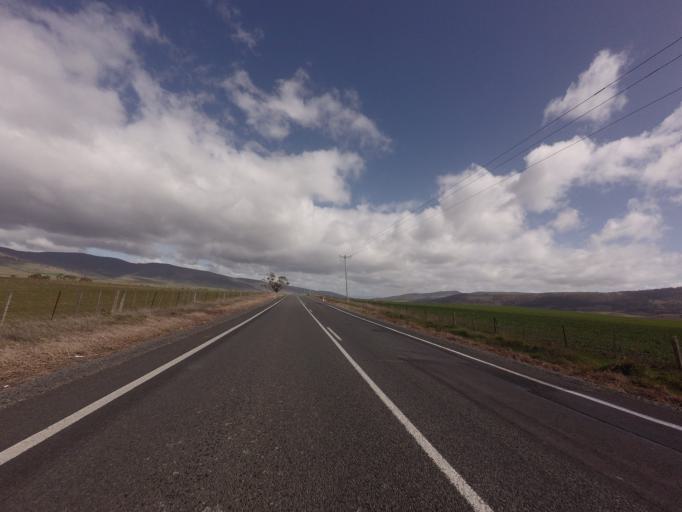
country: AU
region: Tasmania
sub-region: Northern Midlands
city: Evandale
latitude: -41.8007
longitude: 147.6931
